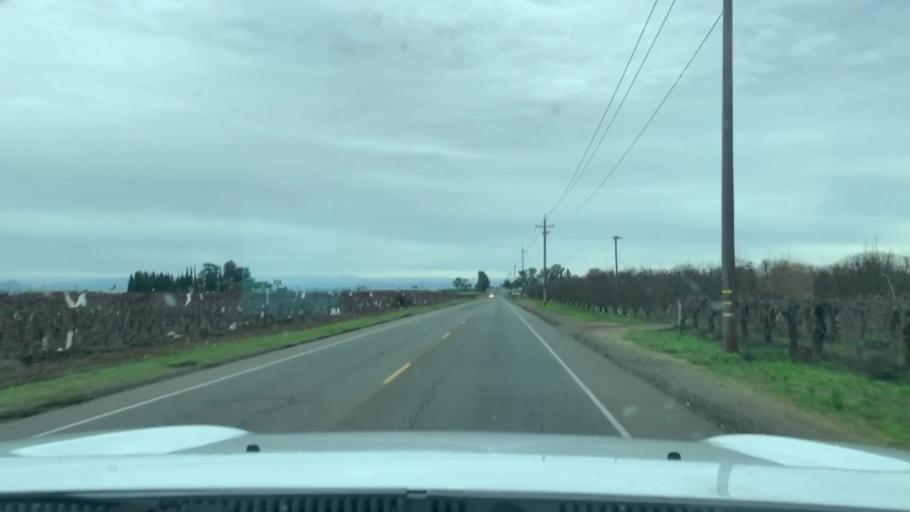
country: US
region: California
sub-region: Fresno County
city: Fowler
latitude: 36.6054
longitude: -119.6719
